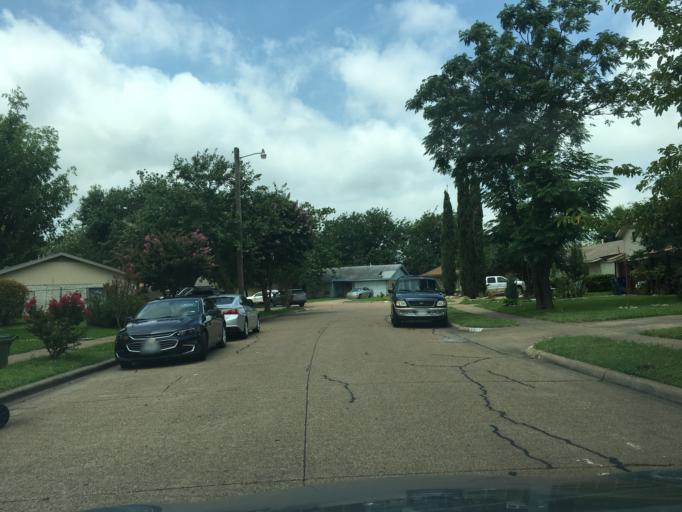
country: US
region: Texas
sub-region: Dallas County
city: Garland
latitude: 32.9203
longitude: -96.6804
